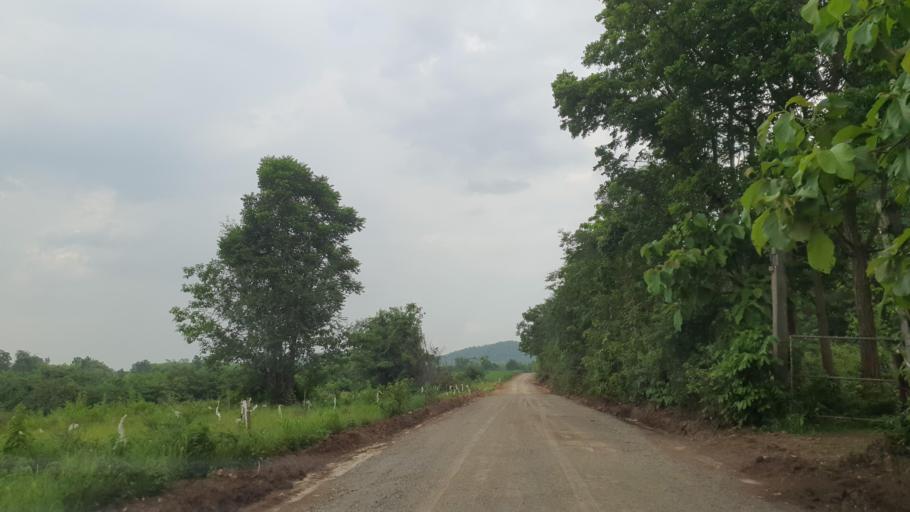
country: TH
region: Sukhothai
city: Thung Saliam
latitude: 17.2582
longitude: 99.5398
